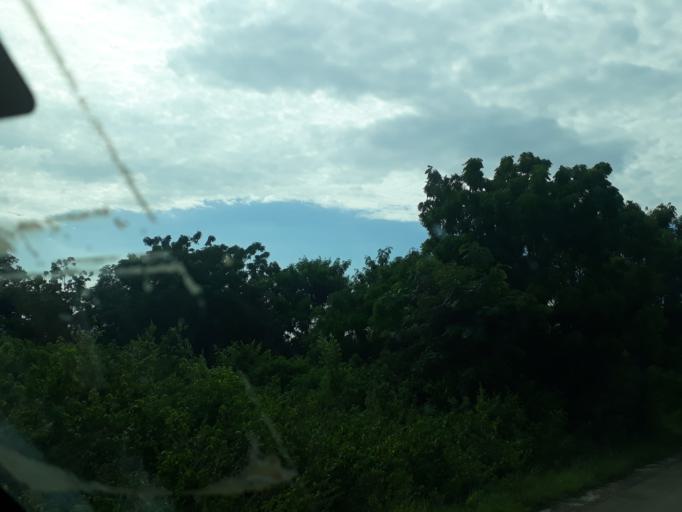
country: TZ
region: Zanzibar North
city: Kijini
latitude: -5.8429
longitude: 39.2839
